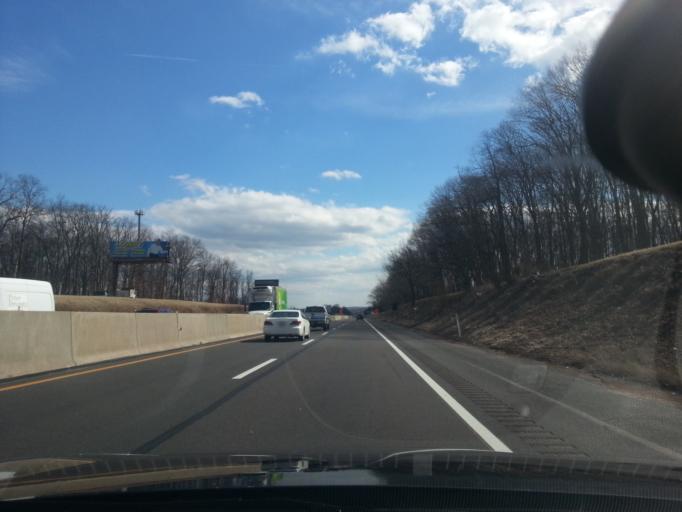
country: US
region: Pennsylvania
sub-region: Montgomery County
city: Harleysville
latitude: 40.2823
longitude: -75.3620
